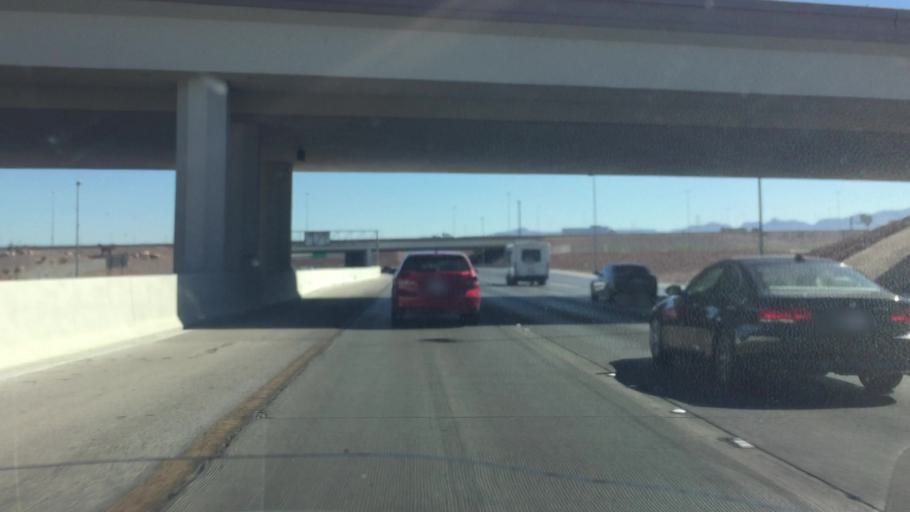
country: US
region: Nevada
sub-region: Clark County
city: Paradise
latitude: 36.0644
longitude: -115.1837
